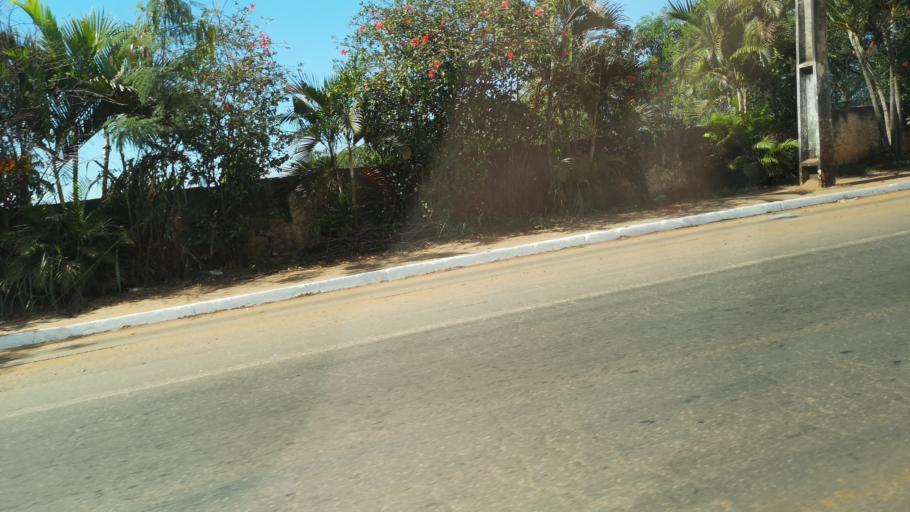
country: BR
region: Goias
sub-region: Senador Canedo
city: Senador Canedo
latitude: -16.7051
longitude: -49.1087
